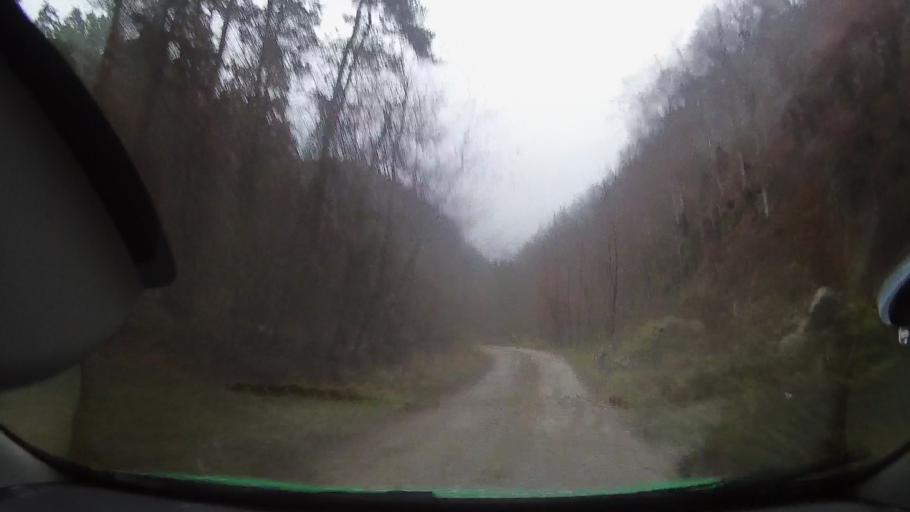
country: RO
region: Alba
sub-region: Comuna Avram Iancu
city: Avram Iancu
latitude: 46.3077
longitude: 22.7697
